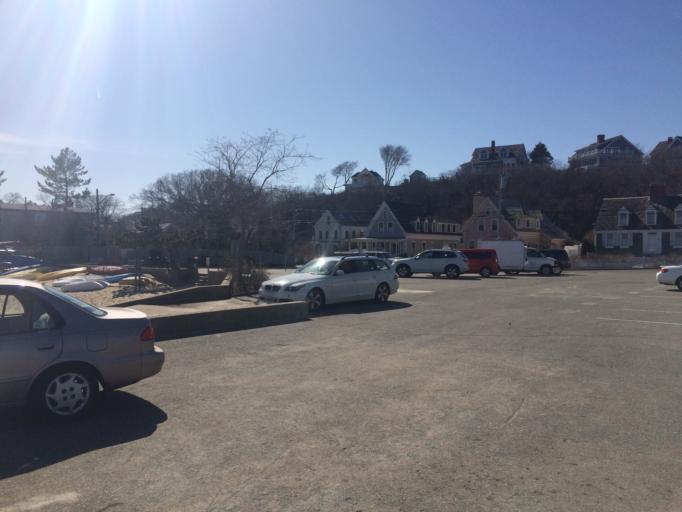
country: US
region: Massachusetts
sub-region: Barnstable County
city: Provincetown
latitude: 42.0418
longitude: -70.1930
